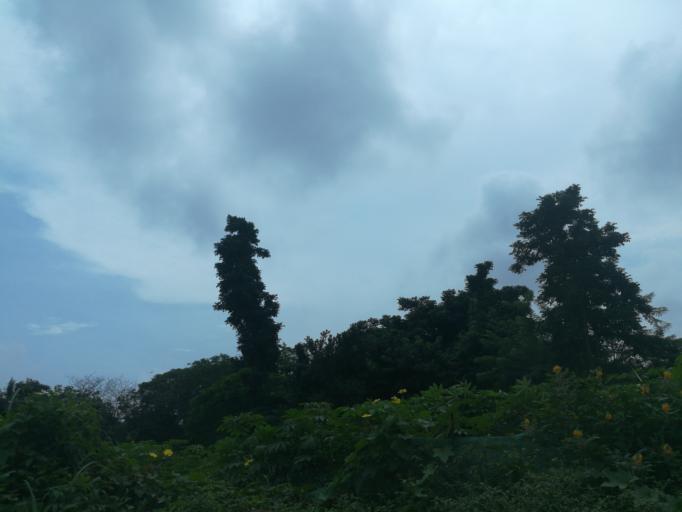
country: NG
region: Lagos
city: Oshodi
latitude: 6.5640
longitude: 3.3576
